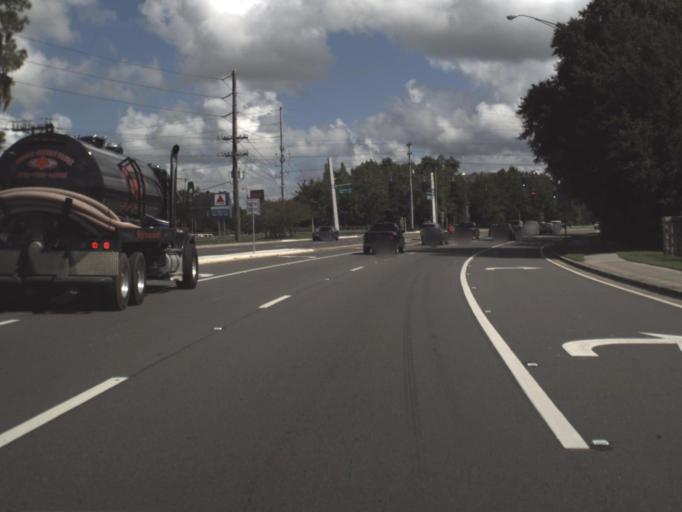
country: US
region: Florida
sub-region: Polk County
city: Lakeland
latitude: 28.0246
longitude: -81.9736
